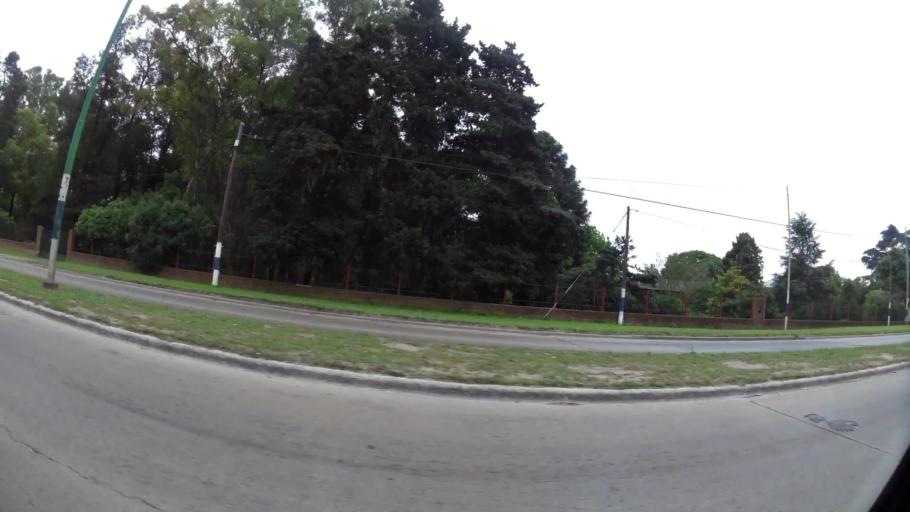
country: AR
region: Buenos Aires
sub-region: Partido de La Plata
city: La Plata
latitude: -34.9639
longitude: -58.0136
